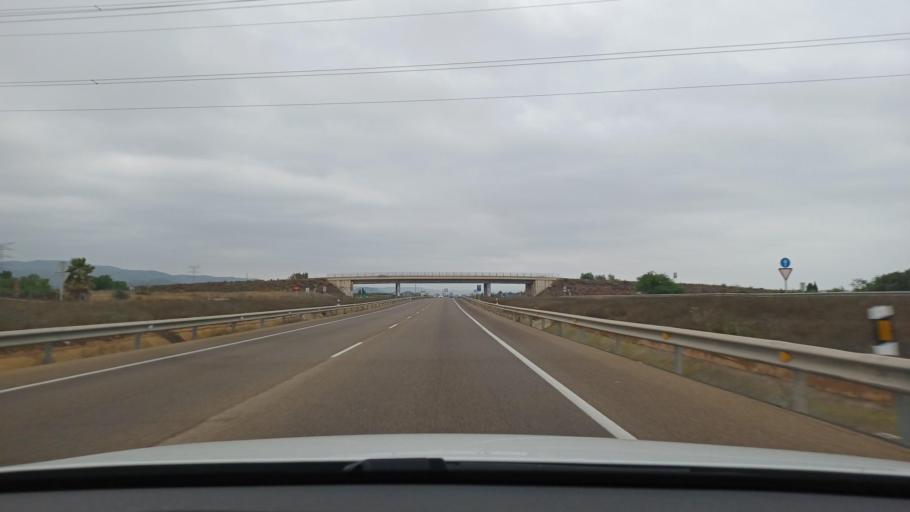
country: ES
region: Valencia
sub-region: Provincia de Castello
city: Orpesa/Oropesa del Mar
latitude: 40.1247
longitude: 0.1446
